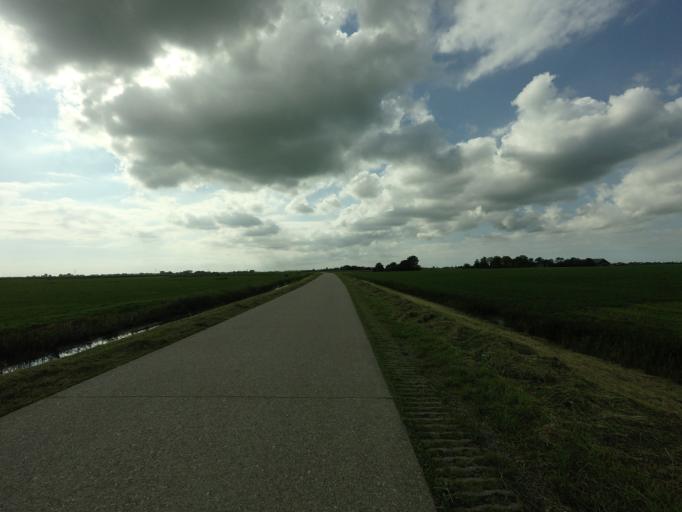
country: NL
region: Friesland
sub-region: Gemeente Littenseradiel
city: Wommels
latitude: 53.0752
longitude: 5.6232
